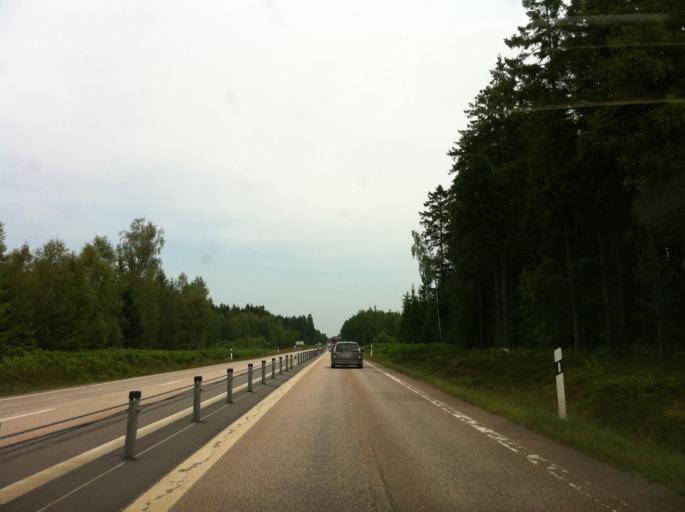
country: SE
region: Blekinge
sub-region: Karlskrona Kommun
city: Jaemjoe
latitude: 56.2487
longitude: 15.9376
